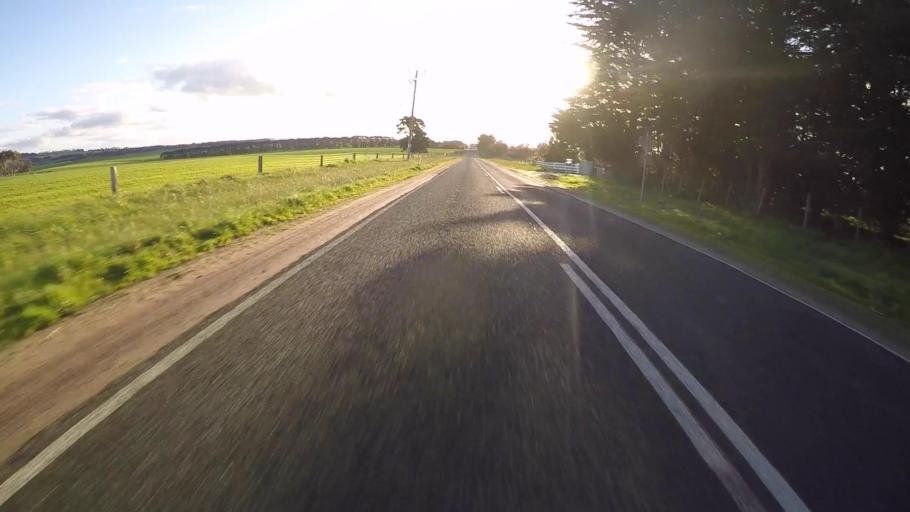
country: AU
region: Victoria
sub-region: Greater Geelong
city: Wandana Heights
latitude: -38.1716
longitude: 144.1856
